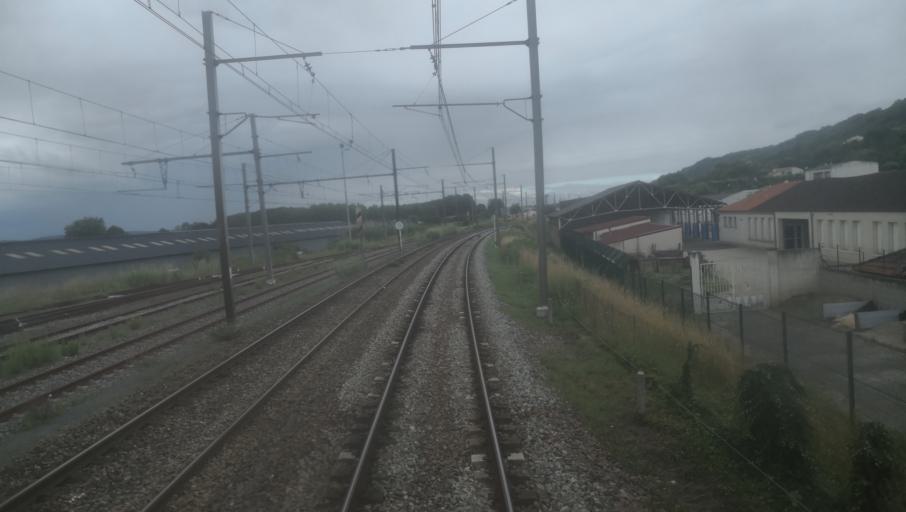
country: FR
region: Aquitaine
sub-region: Departement du Lot-et-Garonne
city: Port-Sainte-Marie
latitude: 44.2511
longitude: 0.3861
